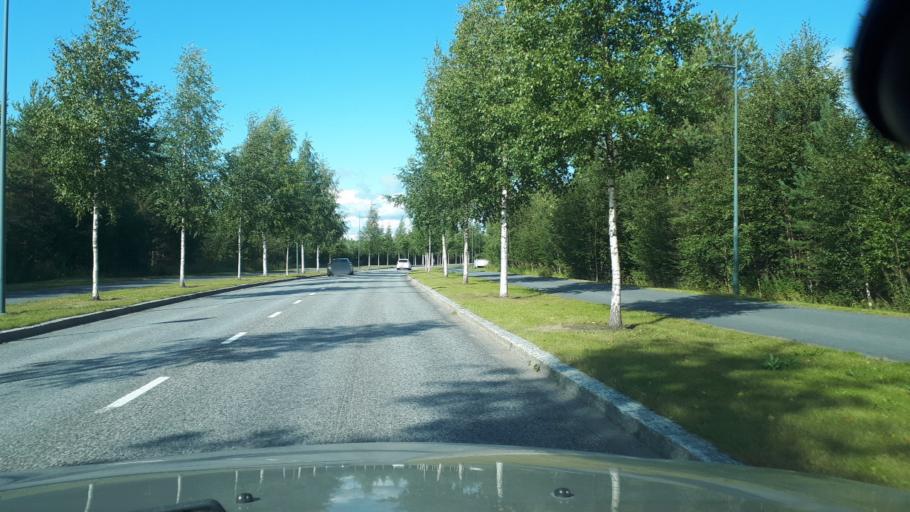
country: FI
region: Northern Ostrobothnia
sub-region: Oulu
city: Oulu
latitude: 65.0694
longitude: 25.4462
